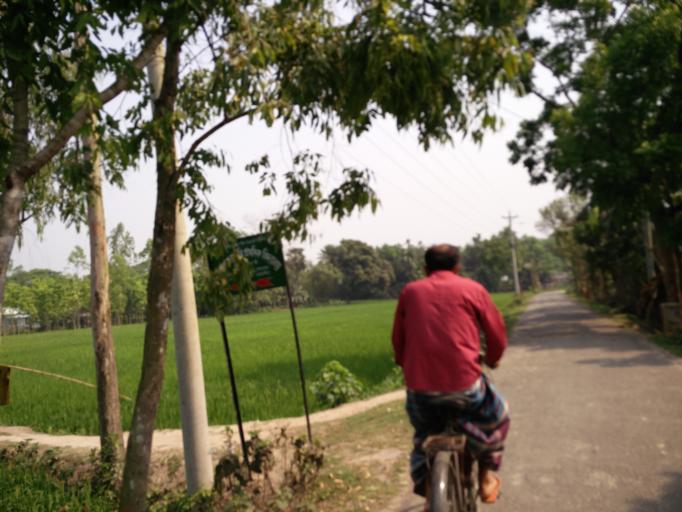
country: BD
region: Dhaka
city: Muktagacha
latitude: 24.9284
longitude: 90.2511
